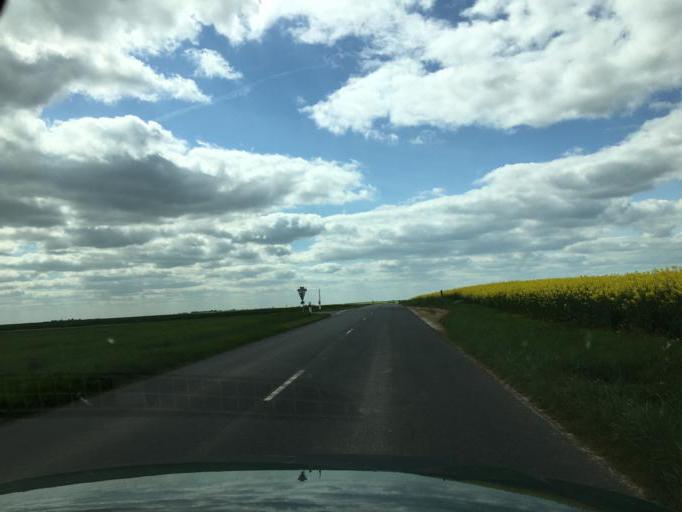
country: FR
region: Centre
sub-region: Departement du Loir-et-Cher
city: Oucques
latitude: 47.8239
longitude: 1.3444
